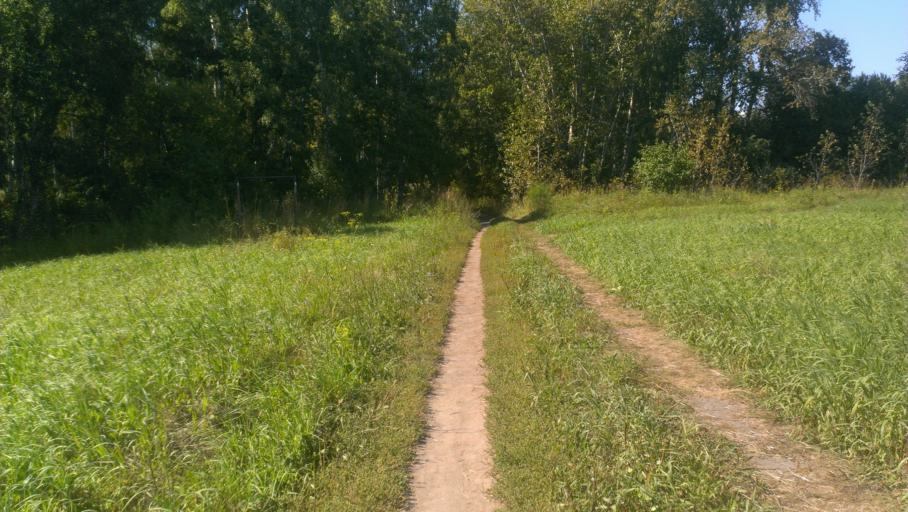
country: RU
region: Altai Krai
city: Nauchnyy Gorodok
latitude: 53.4230
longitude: 83.5128
